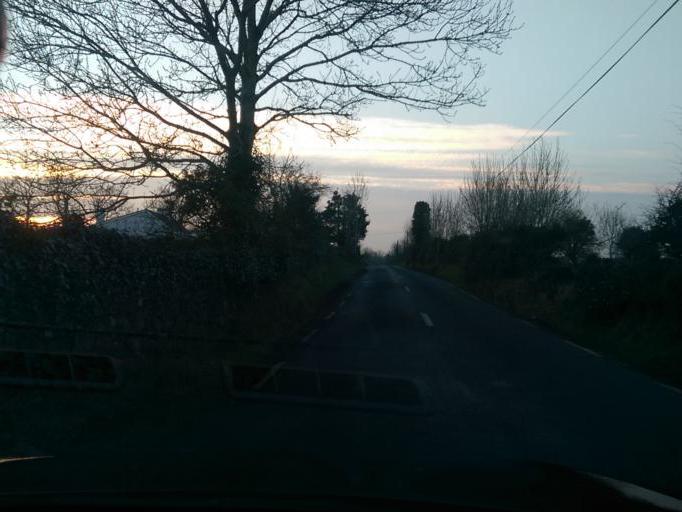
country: IE
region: Connaught
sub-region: County Galway
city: Loughrea
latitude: 53.2340
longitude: -8.6525
